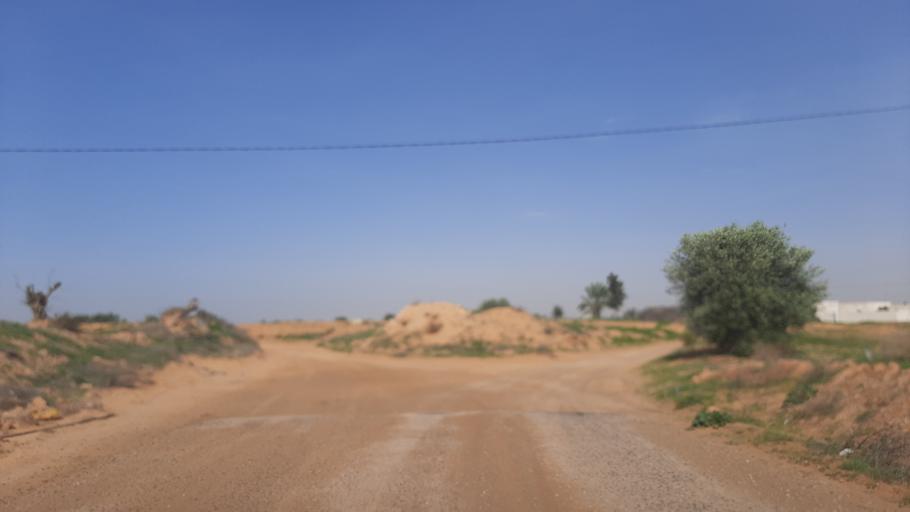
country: TN
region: Madanin
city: Zarzis
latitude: 33.4324
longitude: 10.8087
